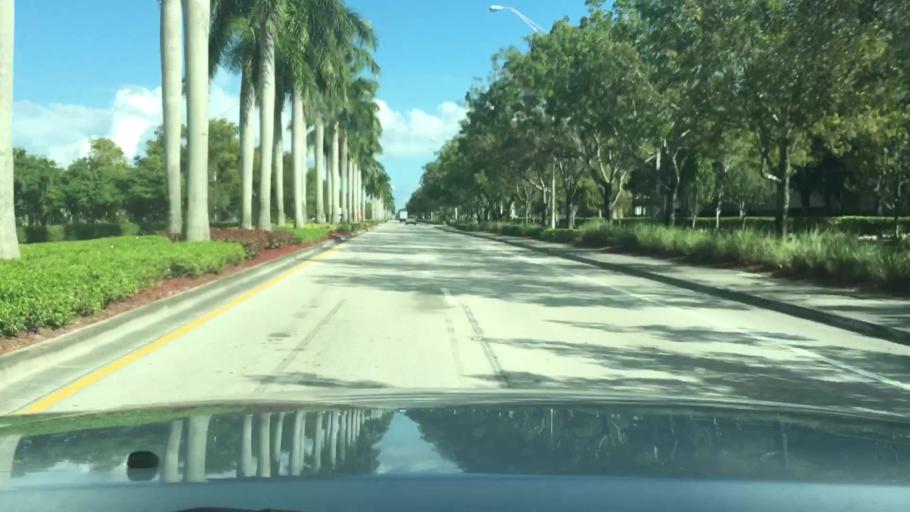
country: US
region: Florida
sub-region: Miami-Dade County
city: Tamiami
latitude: 25.7967
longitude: -80.3970
